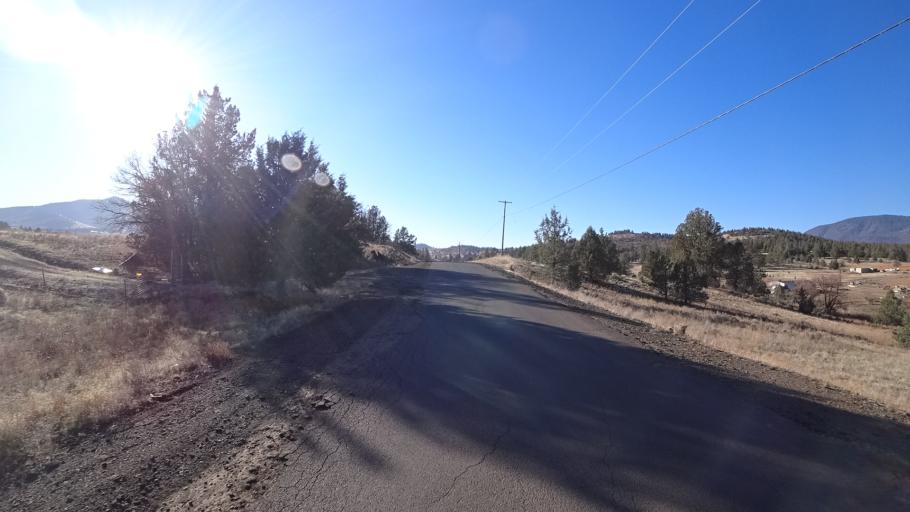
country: US
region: California
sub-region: Siskiyou County
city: Montague
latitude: 41.8919
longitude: -122.4263
